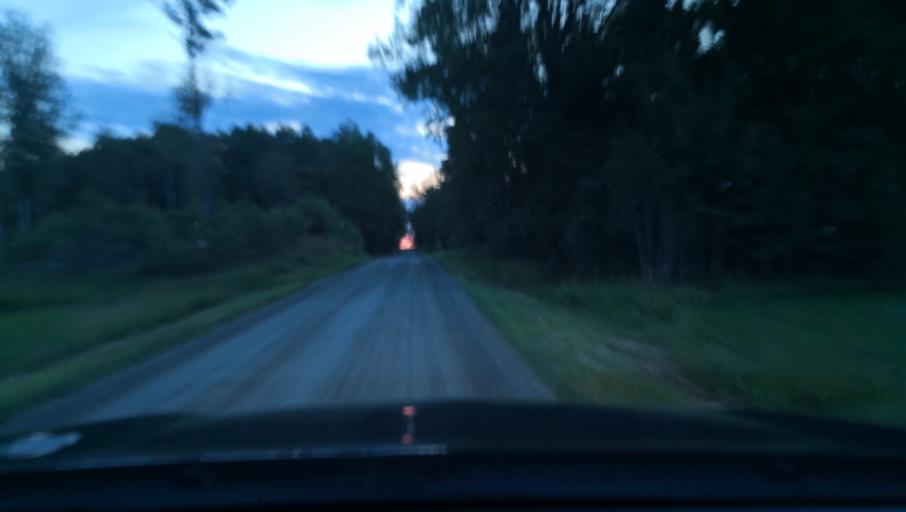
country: SE
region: Uppsala
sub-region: Osthammars Kommun
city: Bjorklinge
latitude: 60.0042
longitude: 17.3403
